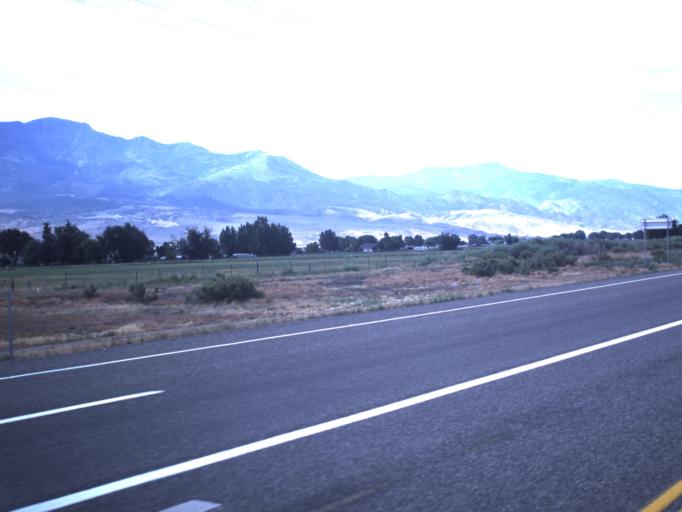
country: US
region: Utah
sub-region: Sevier County
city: Richfield
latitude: 38.7195
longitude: -112.1024
